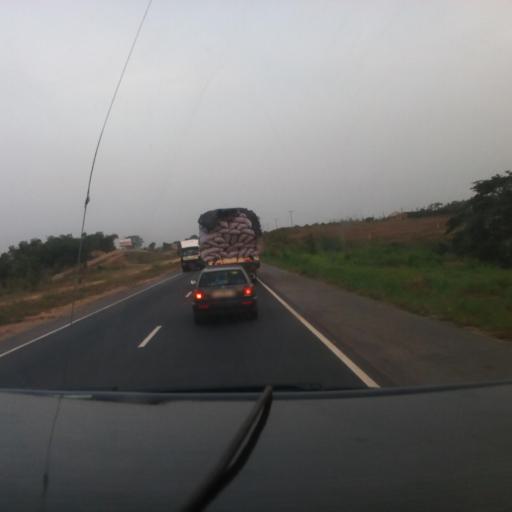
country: GH
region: Eastern
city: Nsawam
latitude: 5.8910
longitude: -0.3820
